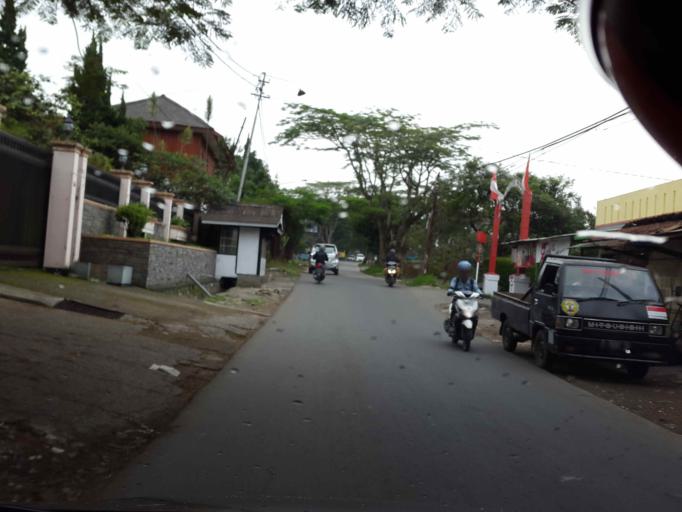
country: ID
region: West Java
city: Lembang
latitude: -6.8182
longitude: 107.6311
